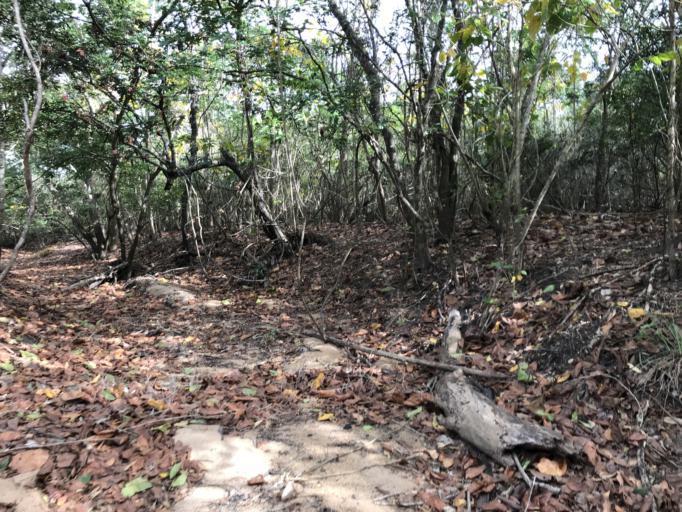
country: LK
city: Padaviya Divisional Secretariat
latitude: 9.0845
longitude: 80.8031
